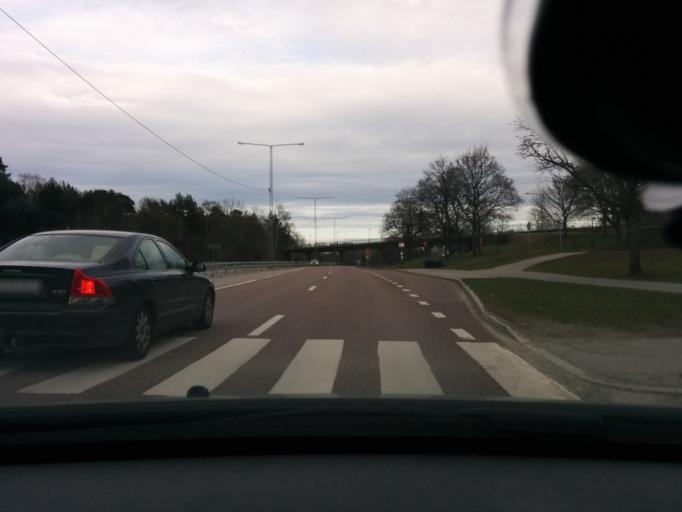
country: SE
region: Stockholm
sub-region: Jarfalla Kommun
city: Jakobsberg
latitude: 59.3690
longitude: 17.8527
